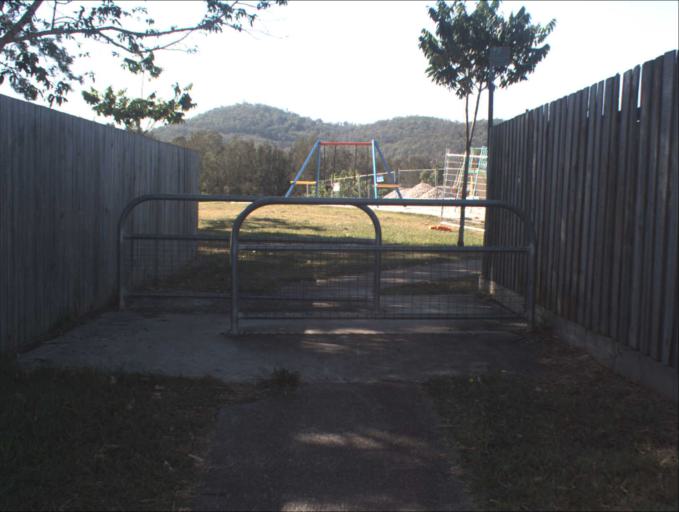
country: AU
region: Queensland
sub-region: Gold Coast
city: Yatala
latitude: -27.7044
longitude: 153.2291
